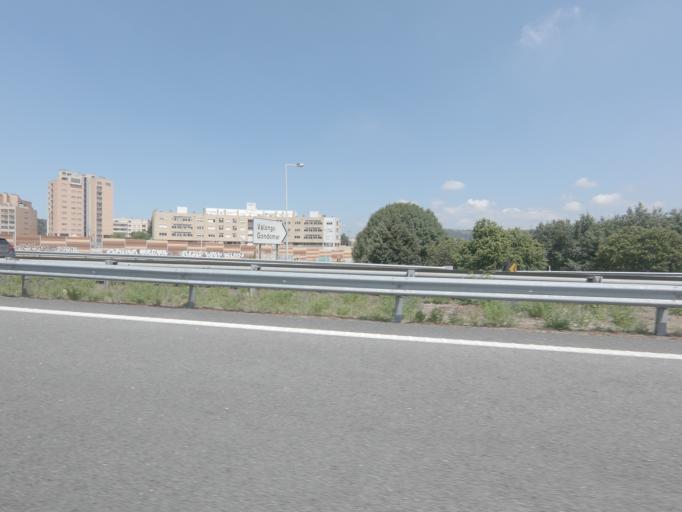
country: PT
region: Porto
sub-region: Valongo
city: Valongo
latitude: 41.1970
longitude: -8.5060
